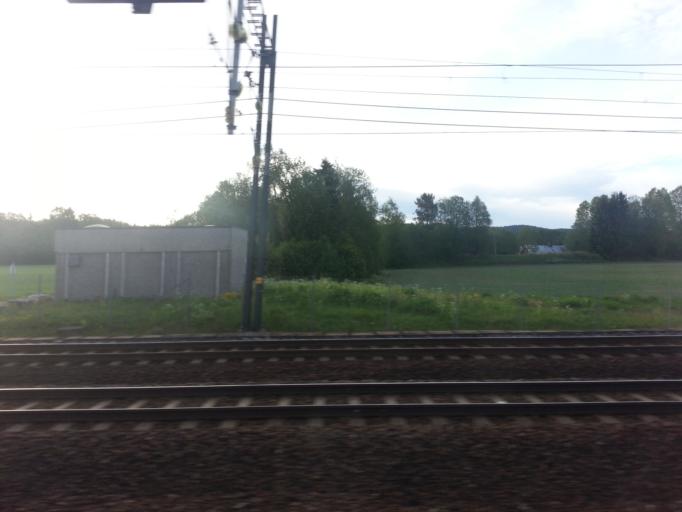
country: NO
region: Akershus
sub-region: Skedsmo
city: Leirsund
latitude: 59.9829
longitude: 11.0742
